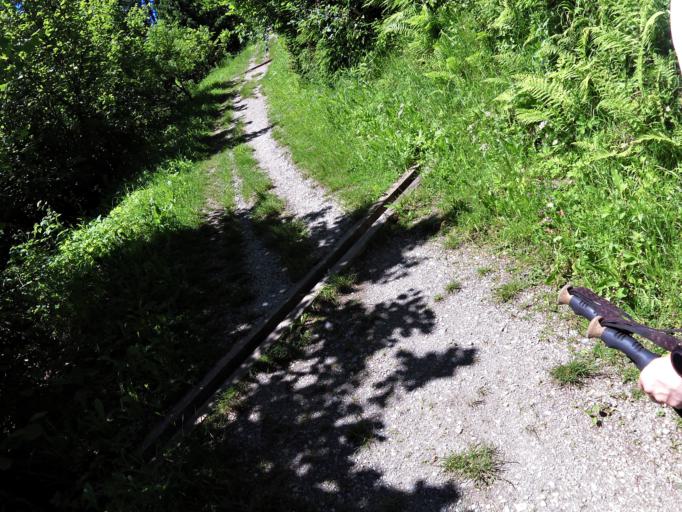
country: AT
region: Tyrol
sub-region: Politischer Bezirk Innsbruck Land
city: Neustift im Stubaital
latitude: 47.1133
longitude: 11.3008
